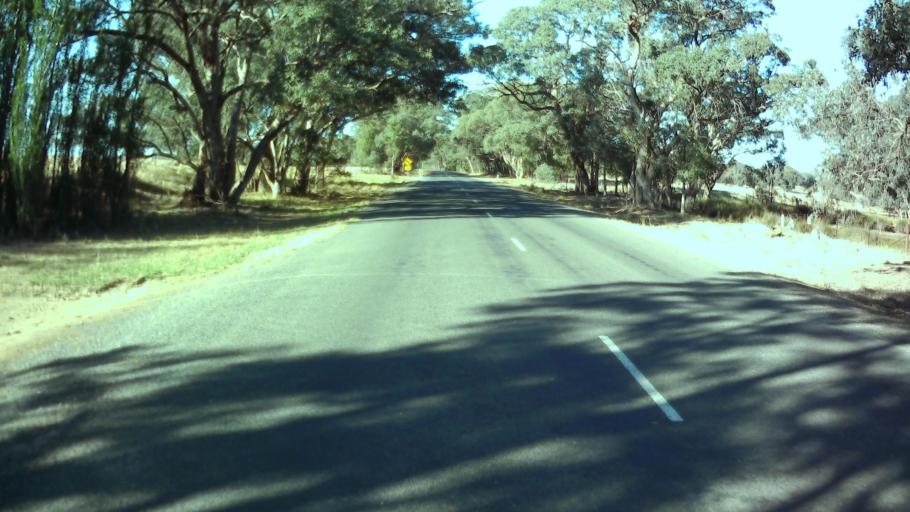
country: AU
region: New South Wales
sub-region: Weddin
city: Grenfell
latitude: -33.9913
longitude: 148.1361
